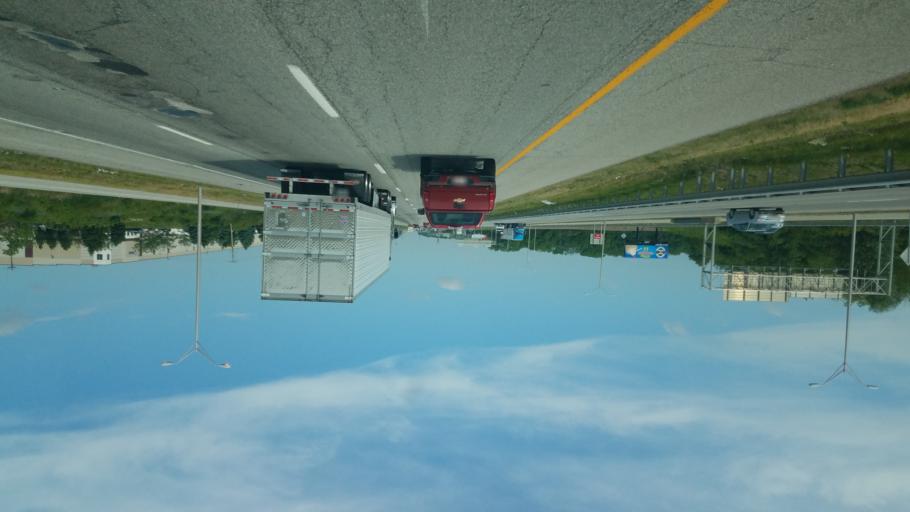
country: US
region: Indiana
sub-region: Hendricks County
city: Plainfield
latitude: 39.6828
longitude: -86.3347
